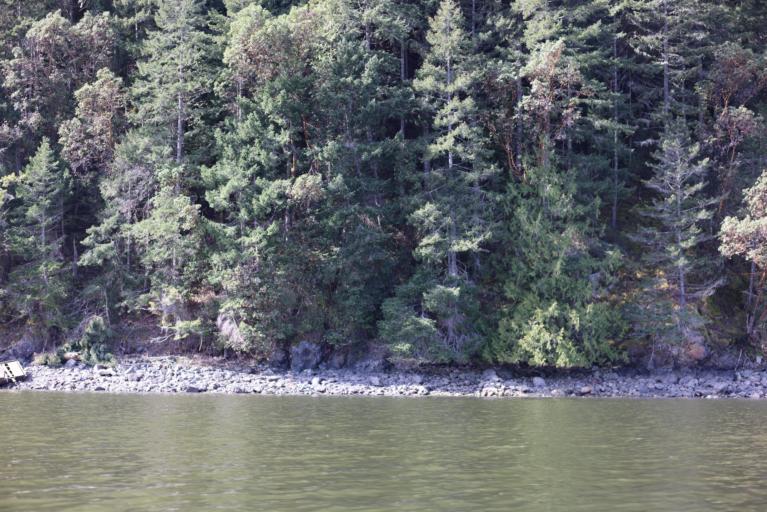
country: CA
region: British Columbia
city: Langford
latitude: 48.5341
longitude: -123.5526
